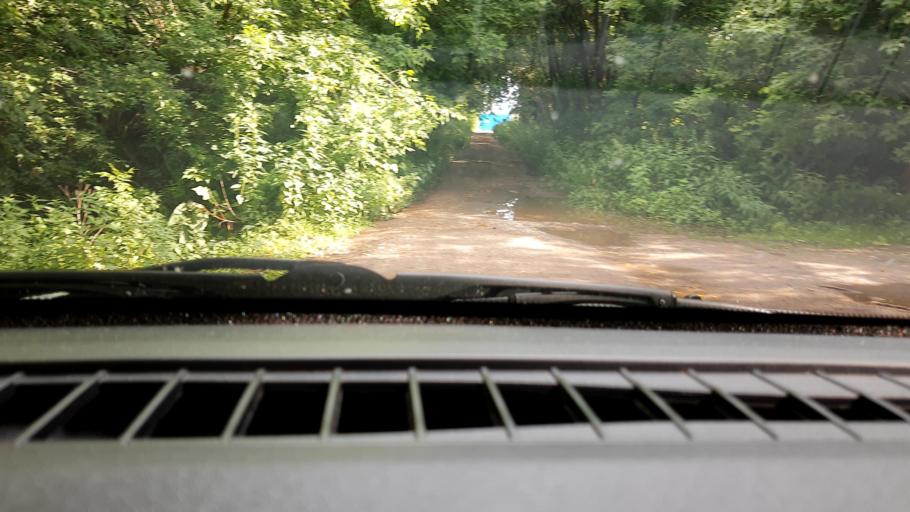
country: RU
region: Nizjnij Novgorod
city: Neklyudovo
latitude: 56.3969
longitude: 43.8501
